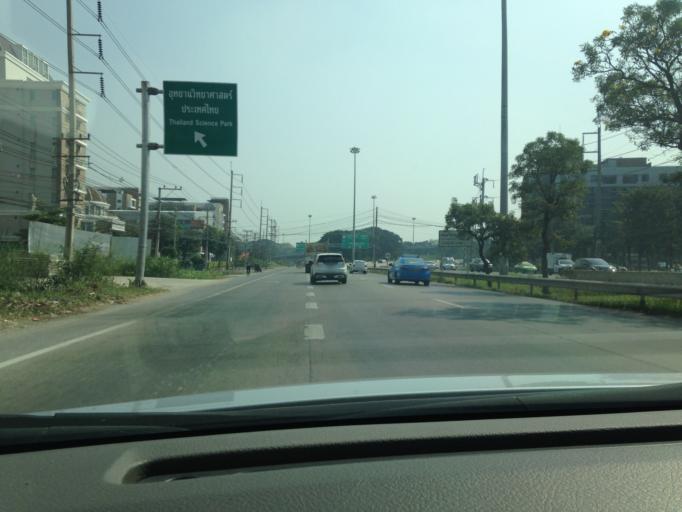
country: TH
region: Pathum Thani
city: Khlong Luang
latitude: 14.0653
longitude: 100.6123
